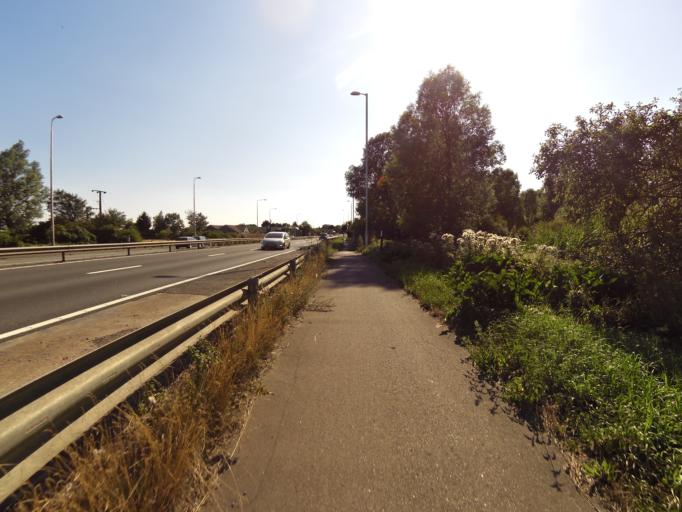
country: GB
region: England
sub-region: Essex
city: Witham
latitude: 51.8195
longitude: 0.6717
